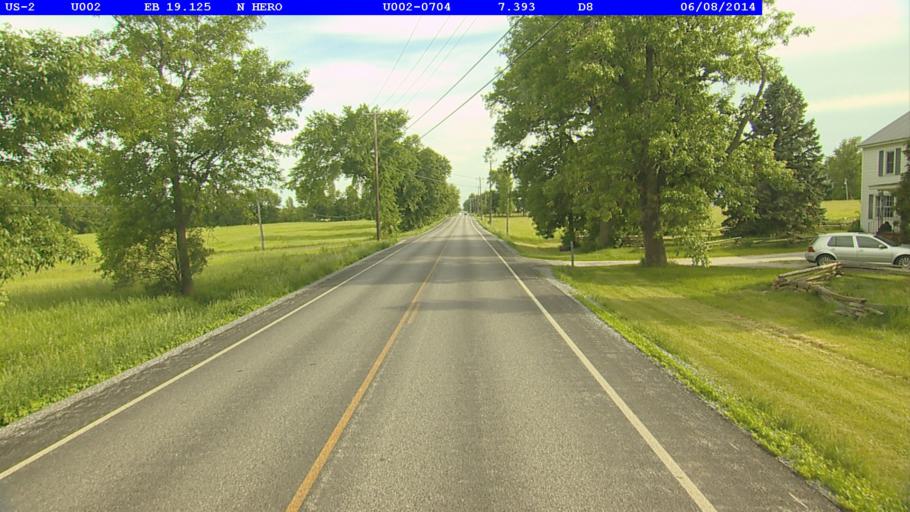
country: US
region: Vermont
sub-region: Grand Isle County
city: North Hero
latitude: 44.7931
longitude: -73.2926
